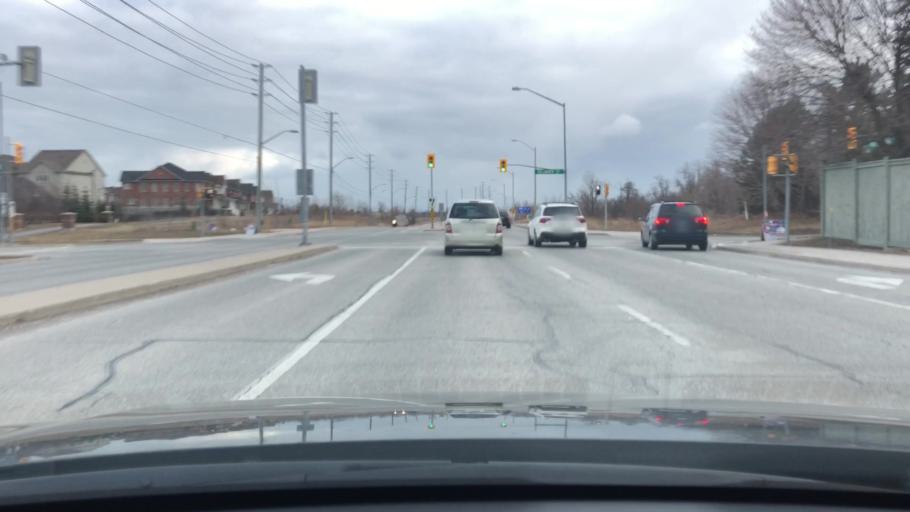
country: CA
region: Ontario
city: Markham
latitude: 43.8761
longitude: -79.2342
